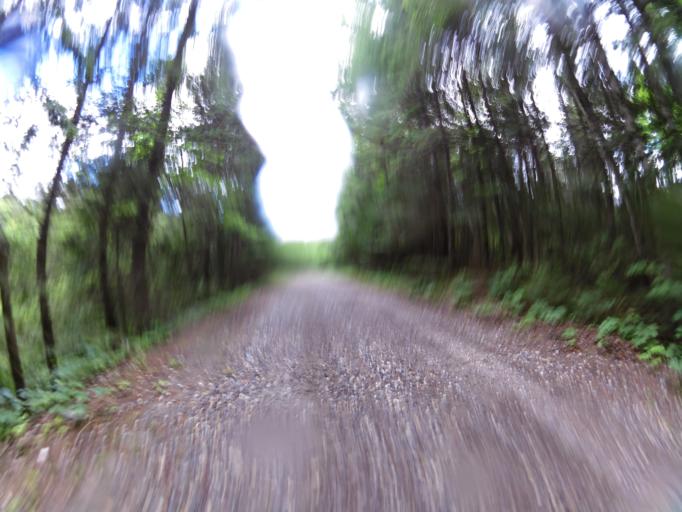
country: CA
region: Ontario
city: Renfrew
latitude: 45.0860
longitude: -76.7208
